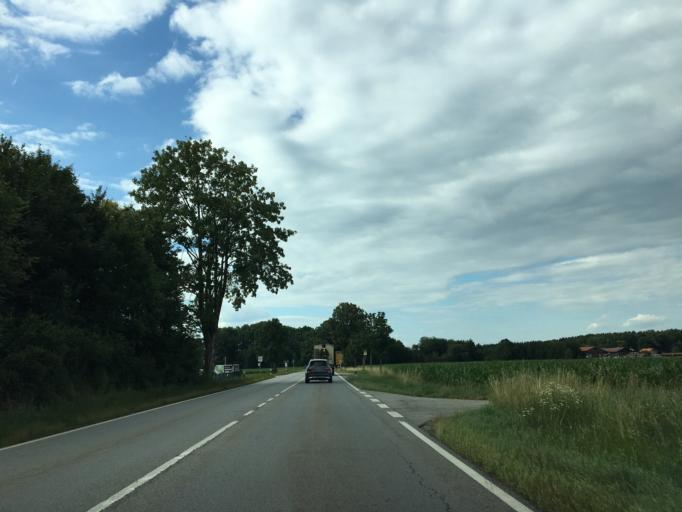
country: DE
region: Bavaria
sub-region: Upper Bavaria
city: Holzkirchen
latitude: 47.8710
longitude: 11.7180
